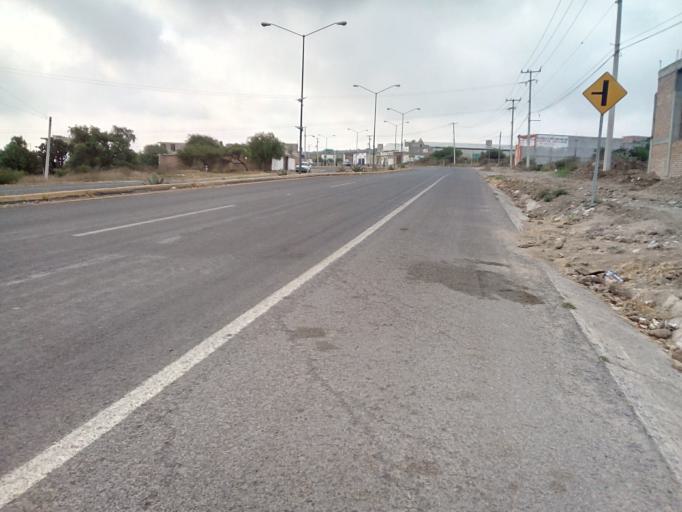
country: MX
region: Guerrero
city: San Luis de la Paz
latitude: 21.2782
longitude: -100.5013
